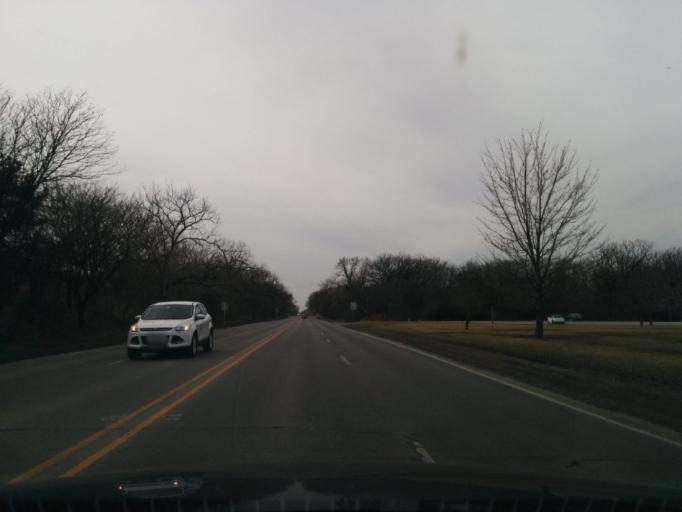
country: US
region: Illinois
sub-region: Cook County
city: Riverside
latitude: 41.8352
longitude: -87.8385
